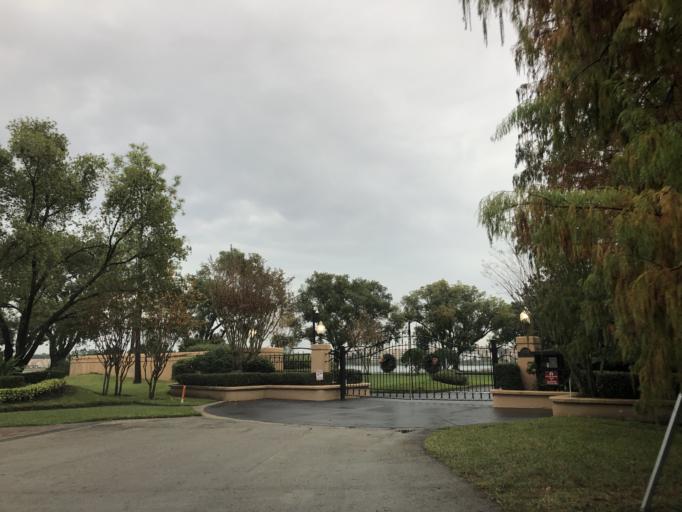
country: US
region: Florida
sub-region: Orange County
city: Doctor Phillips
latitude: 28.4518
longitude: -81.4862
